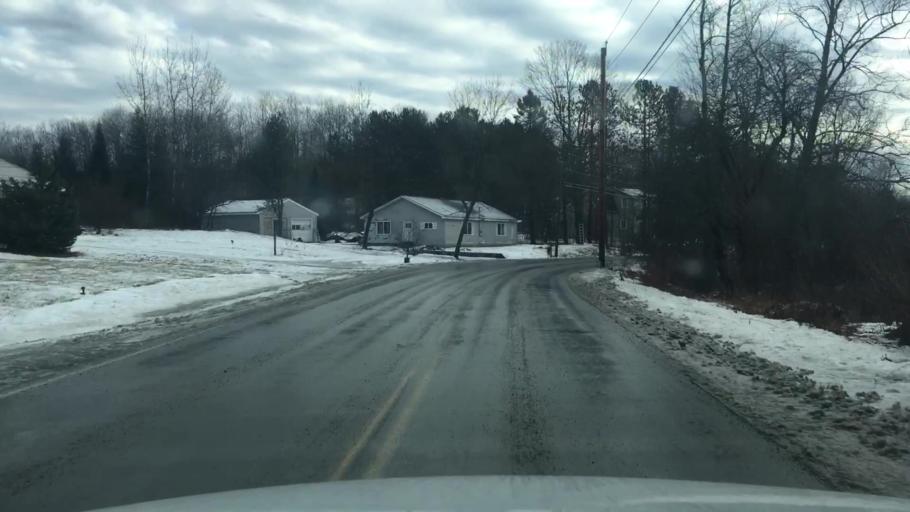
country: US
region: Maine
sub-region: Penobscot County
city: Brewer
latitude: 44.7649
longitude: -68.7778
